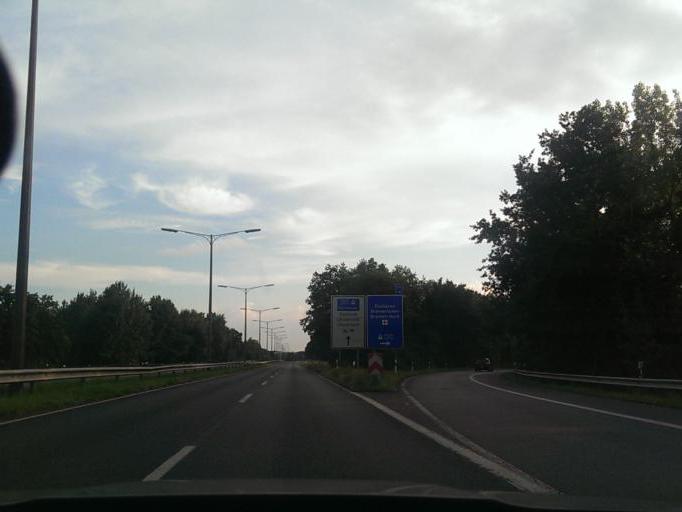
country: DE
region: Lower Saxony
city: Lilienthal
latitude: 53.1133
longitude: 8.8700
